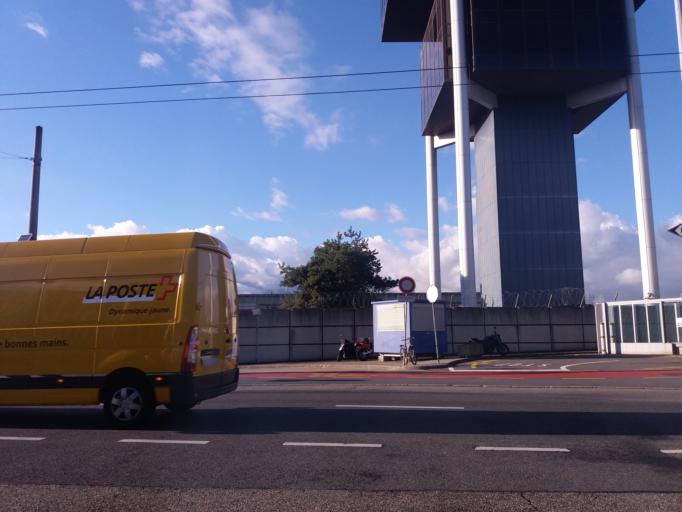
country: CH
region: Geneva
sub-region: Geneva
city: Les Avanchets
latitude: 46.2285
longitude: 6.1039
